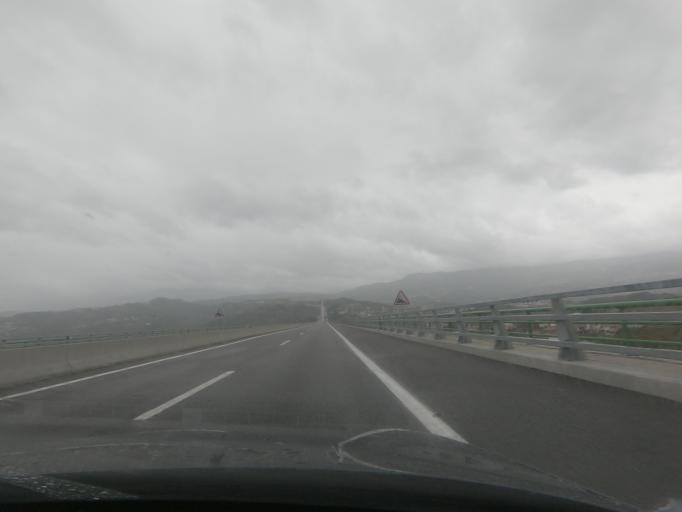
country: PT
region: Vila Real
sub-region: Vila Real
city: Vila Real
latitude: 41.2775
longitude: -7.7373
